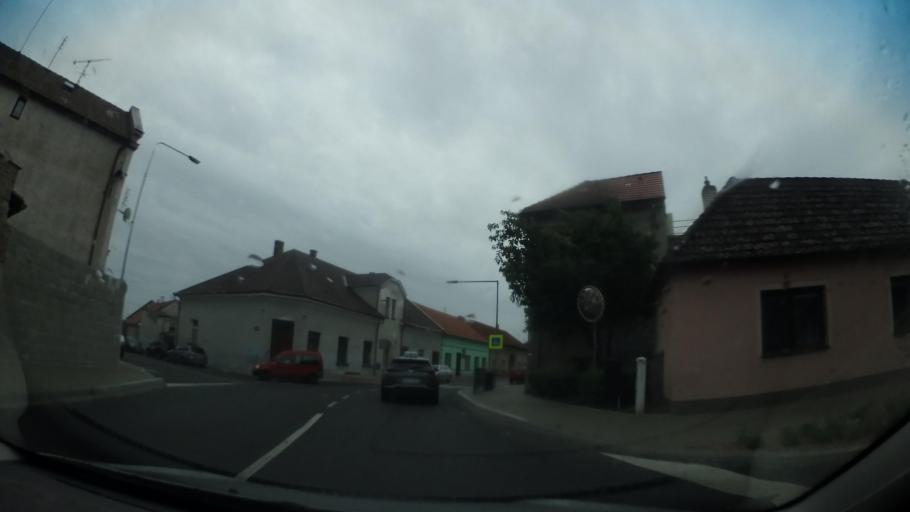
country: CZ
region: Central Bohemia
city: Lysa nad Labem
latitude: 50.2042
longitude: 14.8432
